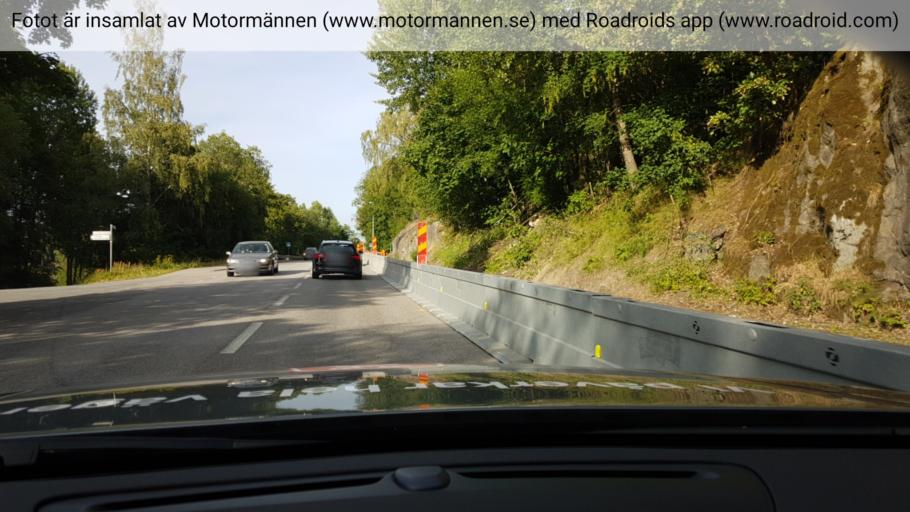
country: SE
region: Stockholm
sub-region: Botkyrka Kommun
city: Tullinge
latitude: 59.2002
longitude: 17.8862
